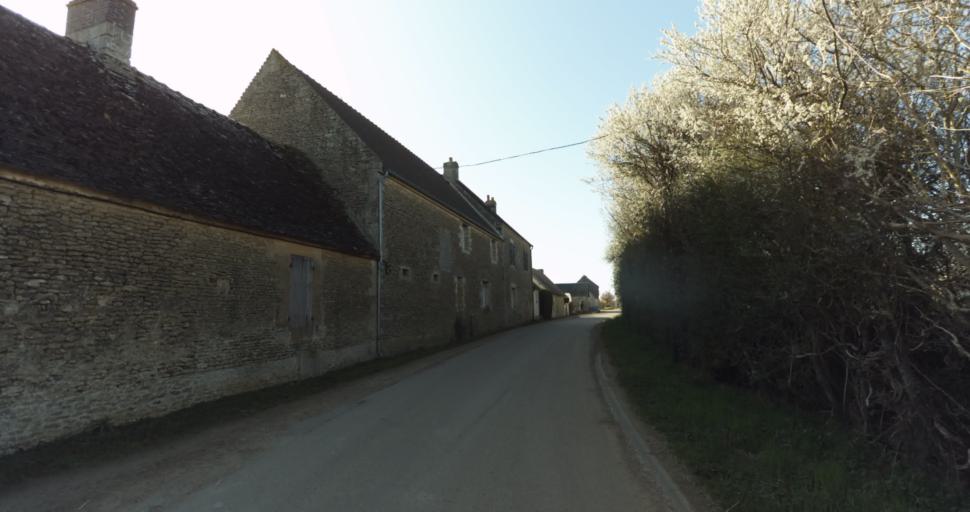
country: FR
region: Lower Normandy
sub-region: Departement du Calvados
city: Saint-Pierre-sur-Dives
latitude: 48.9897
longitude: -0.0248
